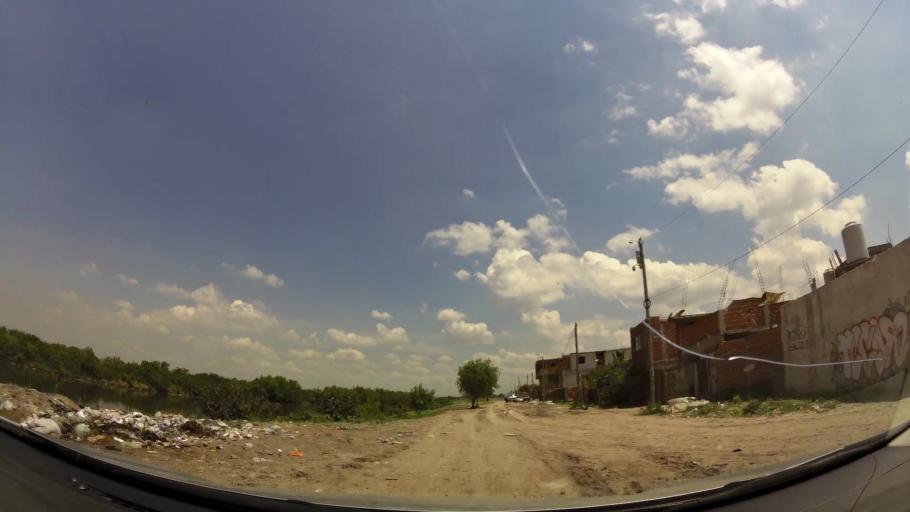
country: AR
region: Buenos Aires
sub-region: Partido de Tigre
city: Tigre
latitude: -34.4536
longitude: -58.5971
